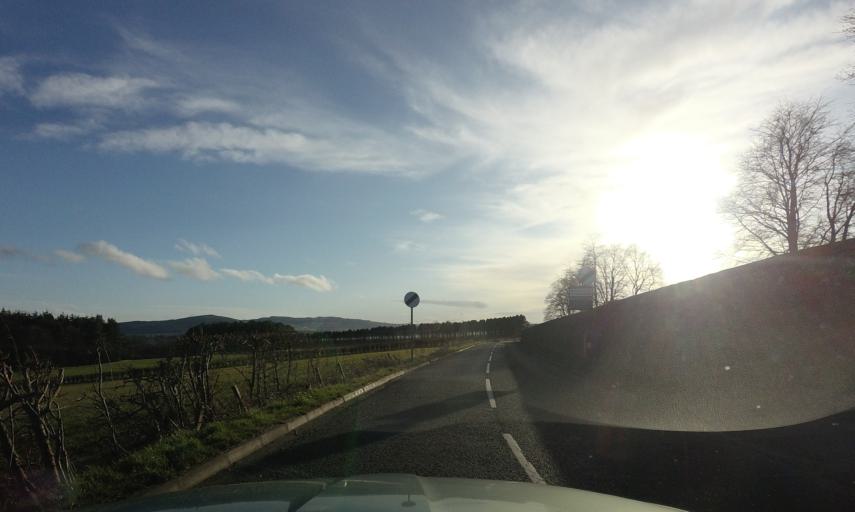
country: GB
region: Scotland
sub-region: Perth and Kinross
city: Errol
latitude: 56.3898
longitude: -3.2155
